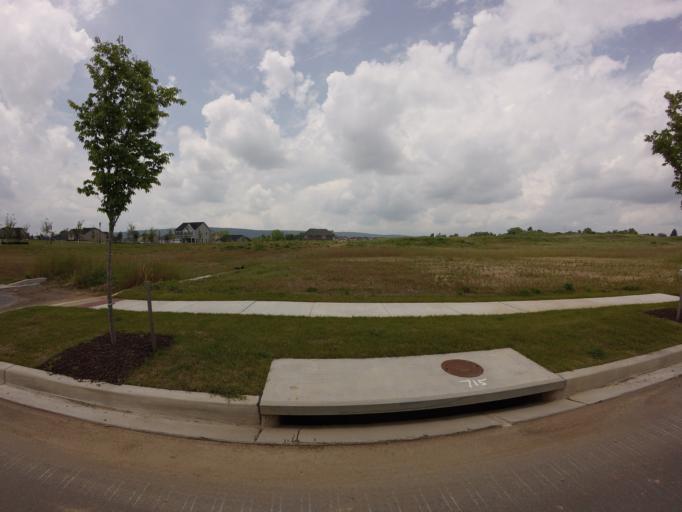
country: US
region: Maryland
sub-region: Frederick County
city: Brunswick
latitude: 39.3259
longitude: -77.6296
